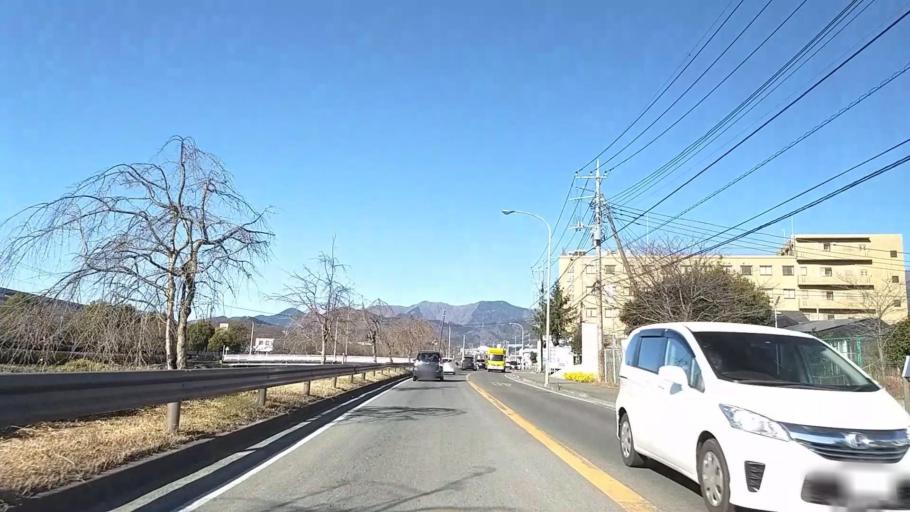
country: JP
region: Kanagawa
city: Hadano
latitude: 35.3848
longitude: 139.1950
